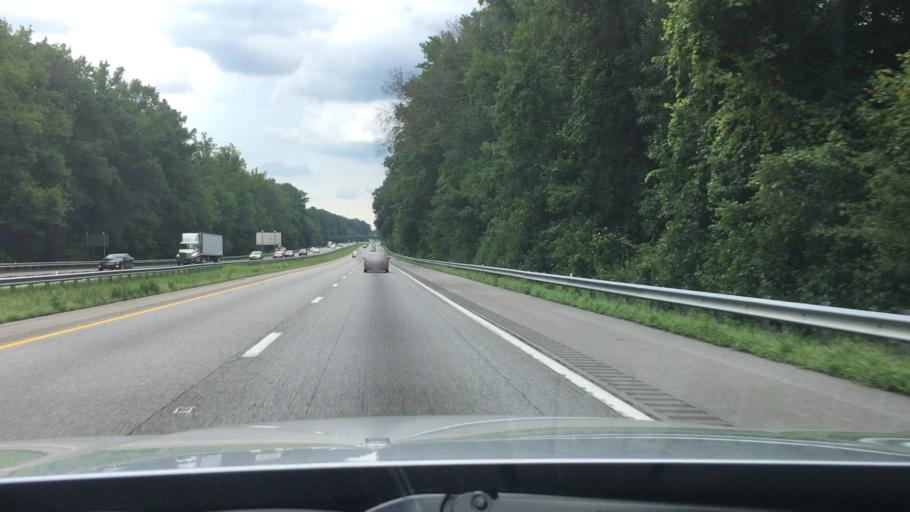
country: US
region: Virginia
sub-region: City of Emporia
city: Emporia
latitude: 36.6776
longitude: -77.5572
